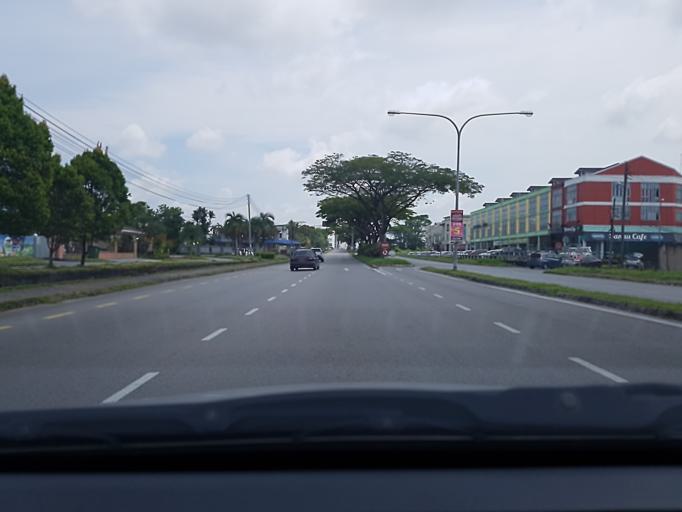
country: MY
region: Sarawak
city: Kuching
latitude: 1.5185
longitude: 110.3611
